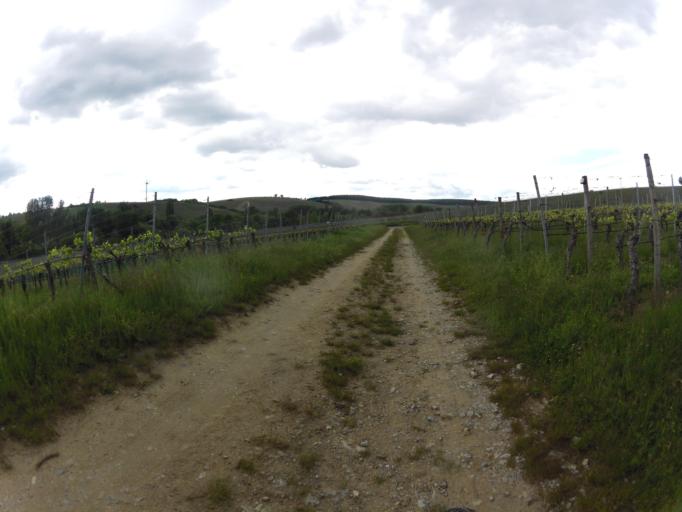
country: DE
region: Bavaria
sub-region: Regierungsbezirk Unterfranken
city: Sommerach
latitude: 49.8342
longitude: 10.1903
